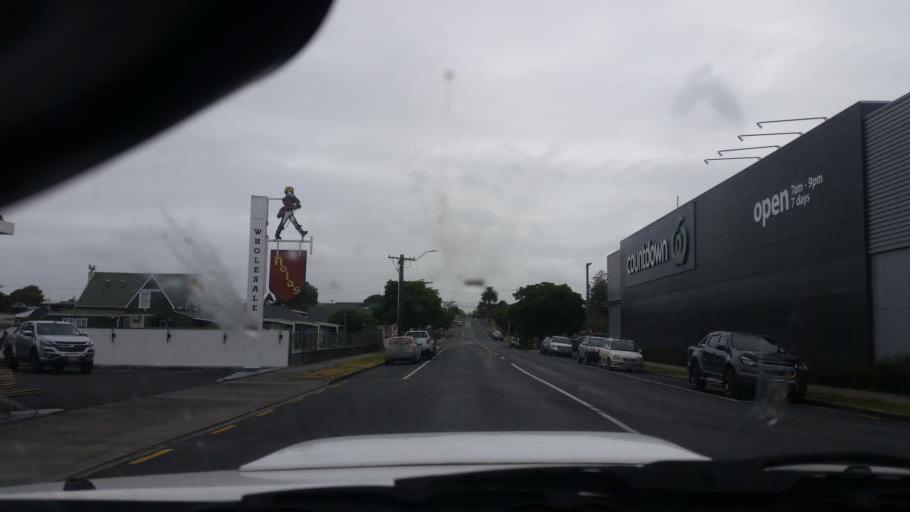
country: NZ
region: Northland
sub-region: Kaipara District
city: Dargaville
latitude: -35.9398
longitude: 173.8717
